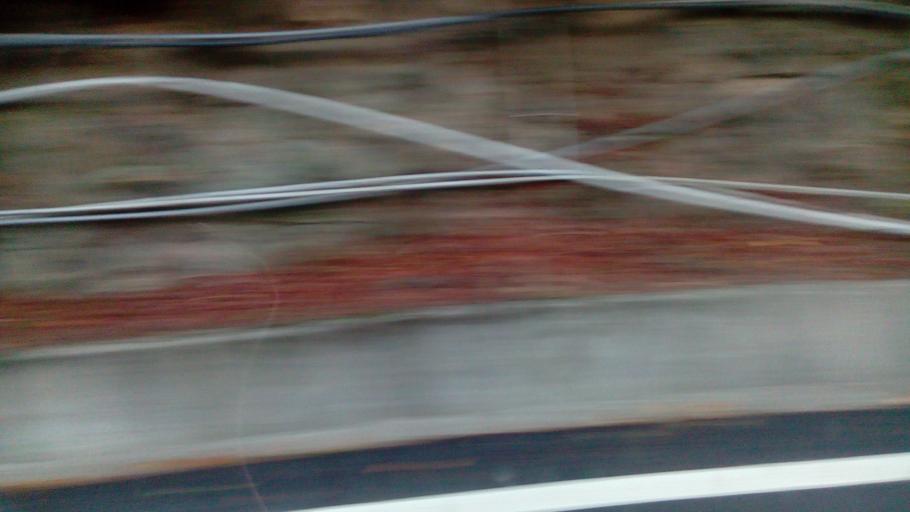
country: TW
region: Taiwan
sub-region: Hualien
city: Hualian
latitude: 24.3267
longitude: 121.3067
